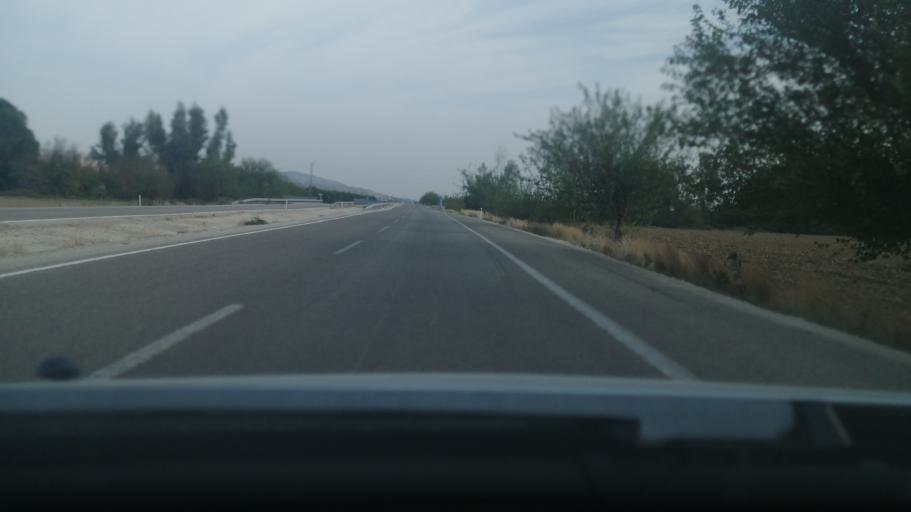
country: TR
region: Adana
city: Kozan
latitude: 37.3871
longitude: 35.8001
